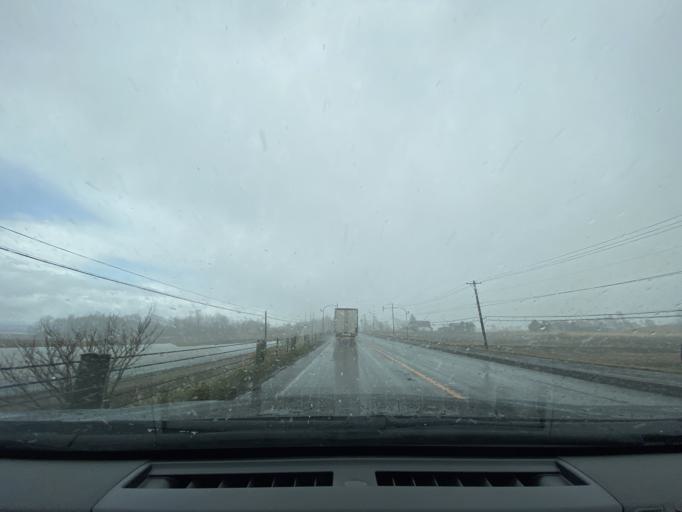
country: JP
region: Hokkaido
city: Fukagawa
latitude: 43.6466
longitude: 141.9595
